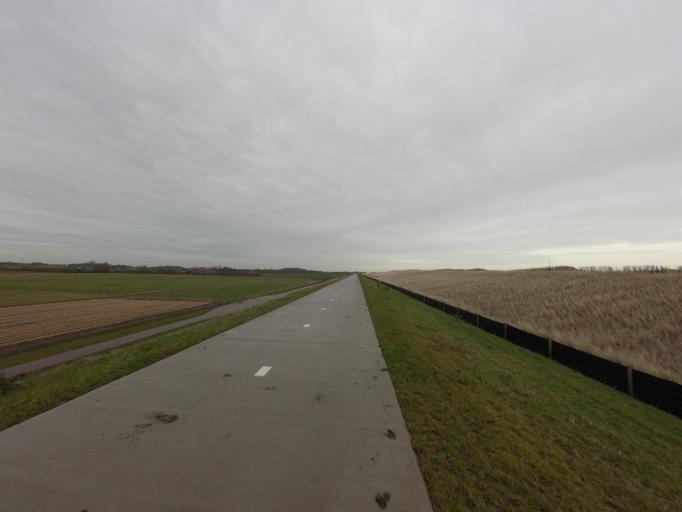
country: NL
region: North Holland
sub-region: Gemeente Texel
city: Den Burg
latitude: 53.0244
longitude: 4.8126
